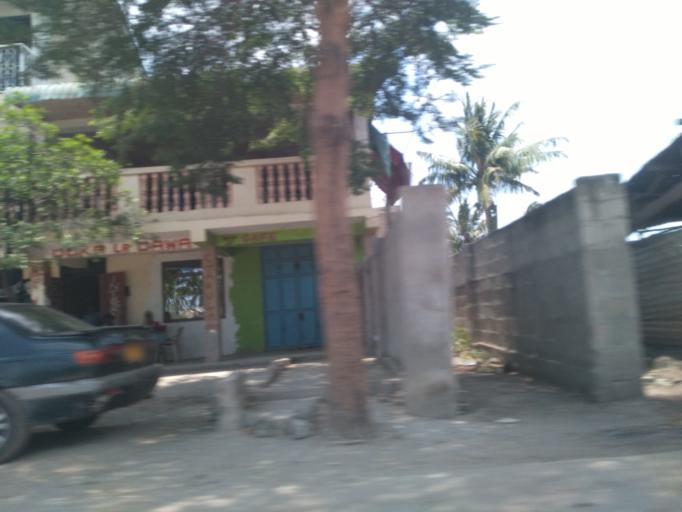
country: TZ
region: Dar es Salaam
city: Dar es Salaam
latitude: -6.8368
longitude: 39.3239
